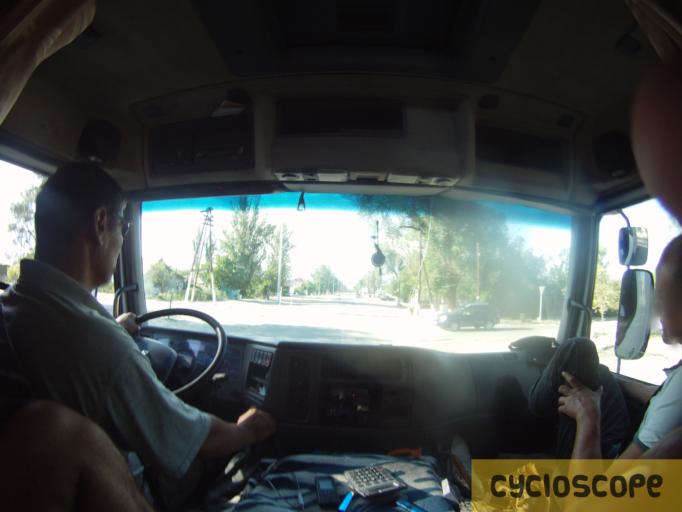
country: KZ
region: Almaty Oblysy
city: Zharkent
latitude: 44.1746
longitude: 79.9931
